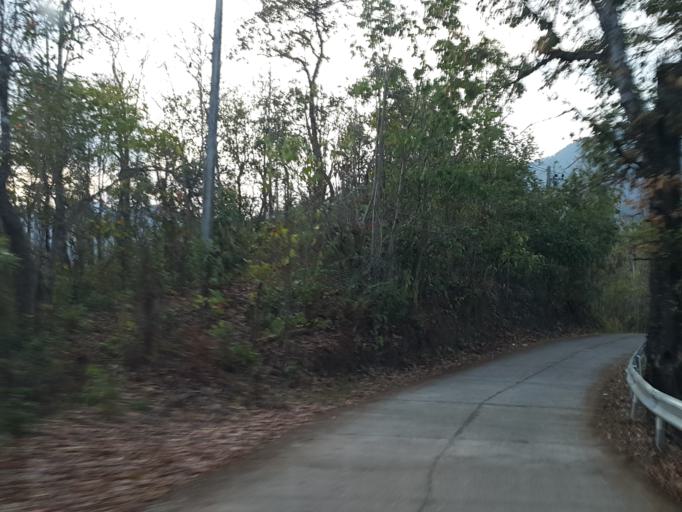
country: TH
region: Lampang
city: Mueang Pan
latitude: 18.8182
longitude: 99.4702
